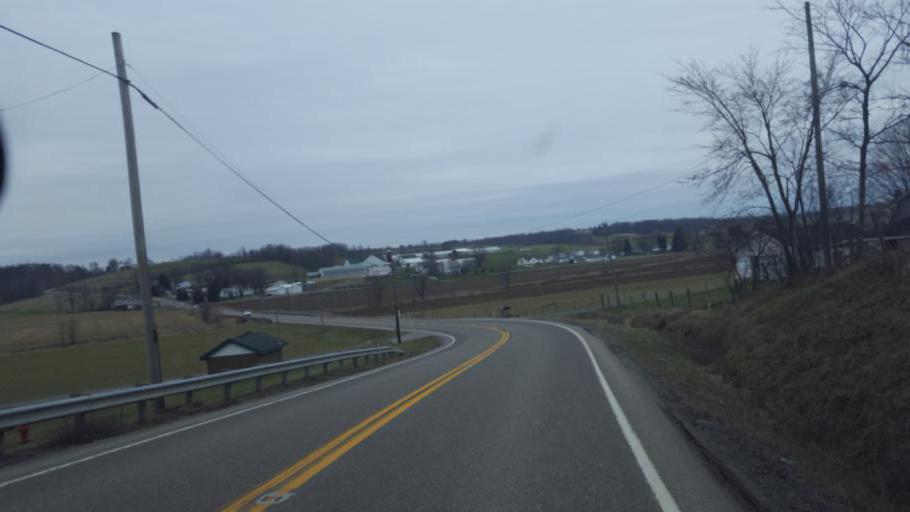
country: US
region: Ohio
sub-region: Tuscarawas County
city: Sugarcreek
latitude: 40.5463
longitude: -81.7210
